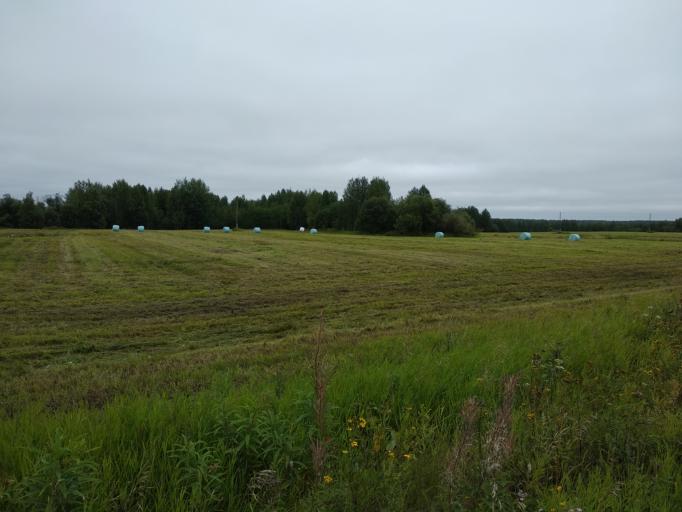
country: RU
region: Sverdlovsk
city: Serov
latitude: 59.8485
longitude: 60.5860
